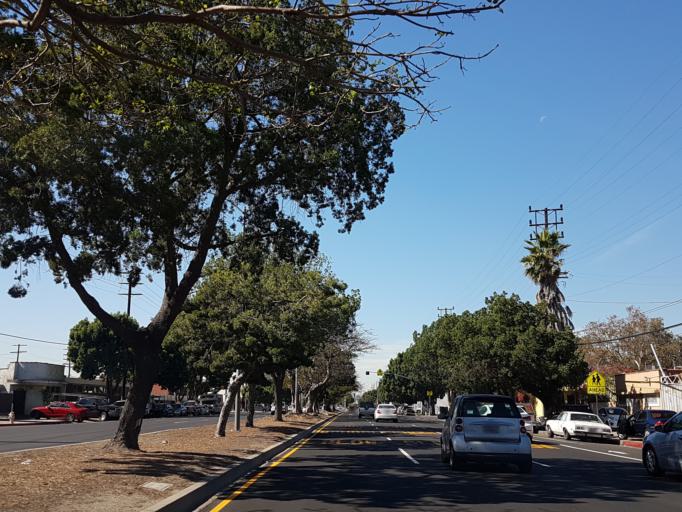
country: US
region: California
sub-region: Los Angeles County
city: West Hollywood
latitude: 34.0446
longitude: -118.3551
